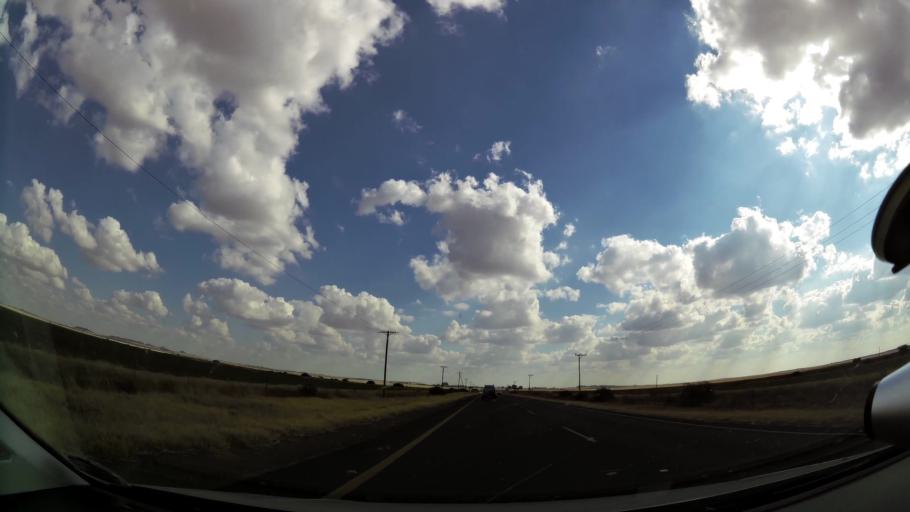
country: ZA
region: Orange Free State
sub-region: Xhariep District Municipality
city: Koffiefontein
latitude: -29.1305
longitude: 25.5193
